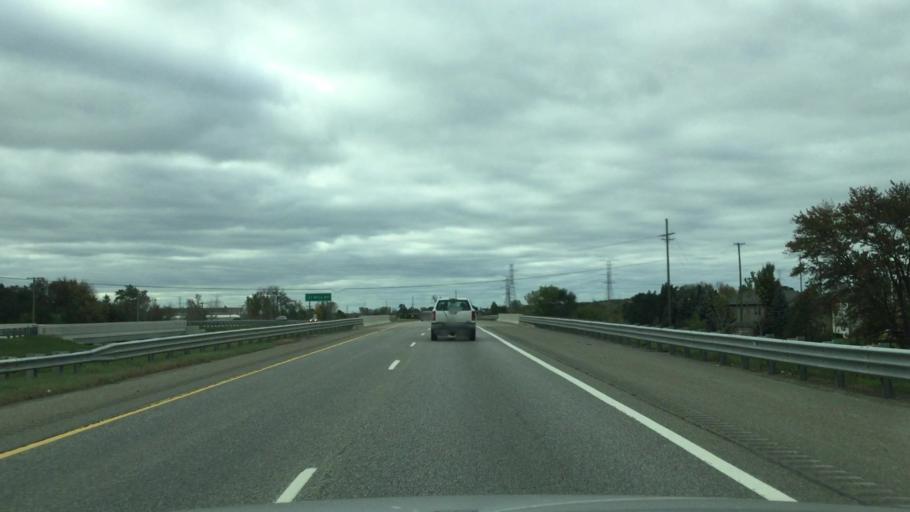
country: US
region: Michigan
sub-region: Macomb County
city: Romeo
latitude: 42.7876
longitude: -83.0053
